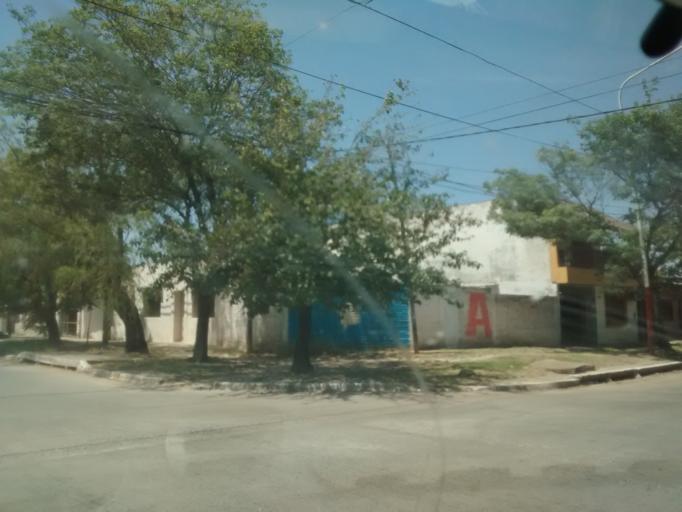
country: AR
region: Chaco
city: Resistencia
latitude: -27.4438
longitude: -59.0070
